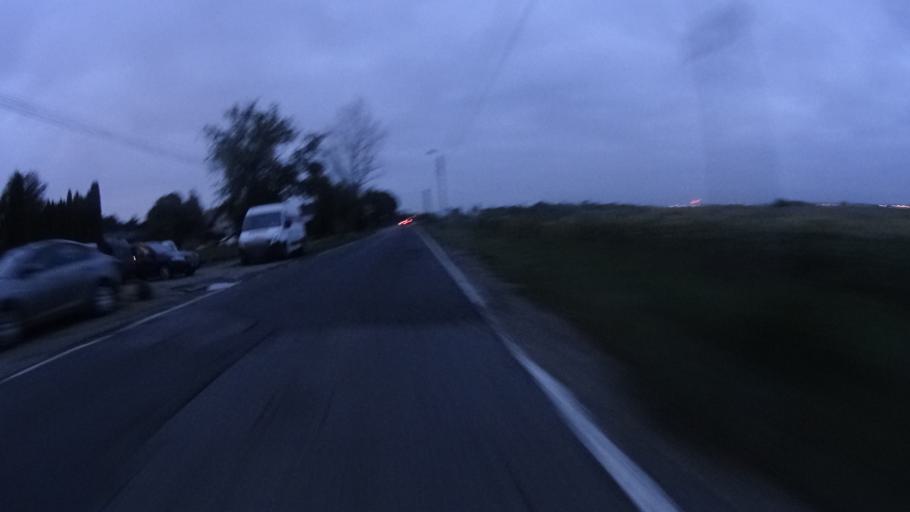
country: PL
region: Masovian Voivodeship
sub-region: Powiat warszawski zachodni
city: Babice
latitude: 52.2290
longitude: 20.8698
